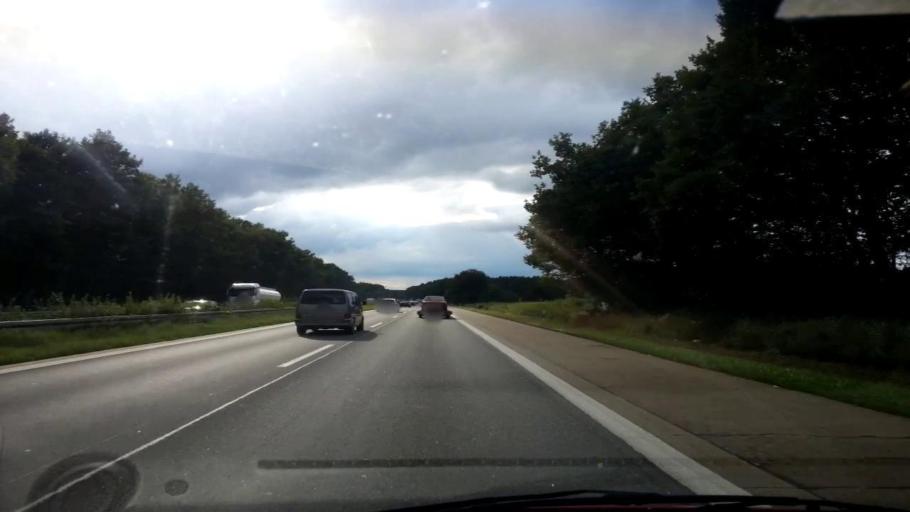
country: DE
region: Bavaria
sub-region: Regierungsbezirk Mittelfranken
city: Muhlhausen
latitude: 49.7377
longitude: 10.7710
